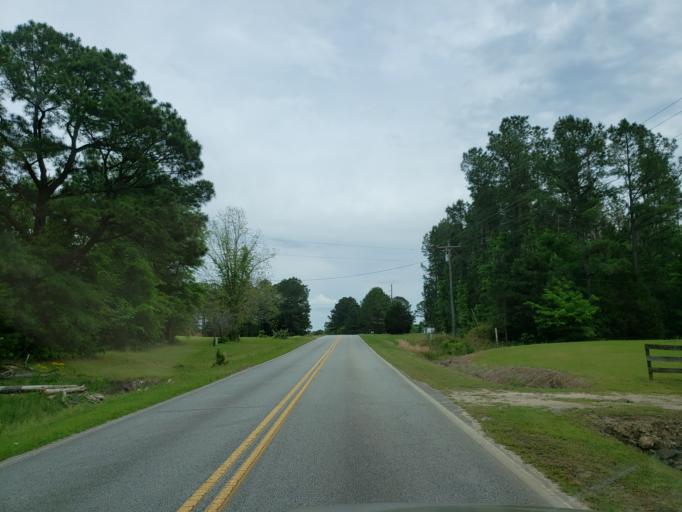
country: US
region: Georgia
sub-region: Bibb County
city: West Point
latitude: 32.8221
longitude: -83.8690
